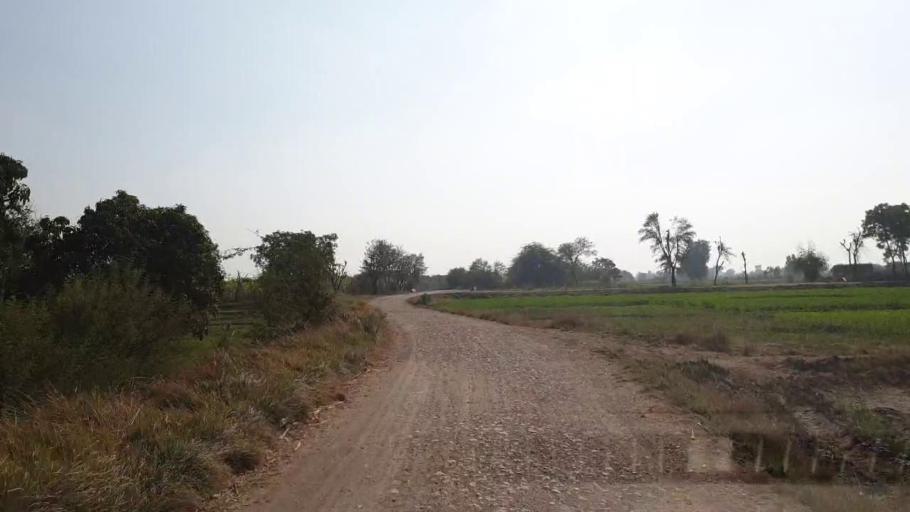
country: PK
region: Sindh
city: Tando Adam
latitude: 25.6796
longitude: 68.5661
